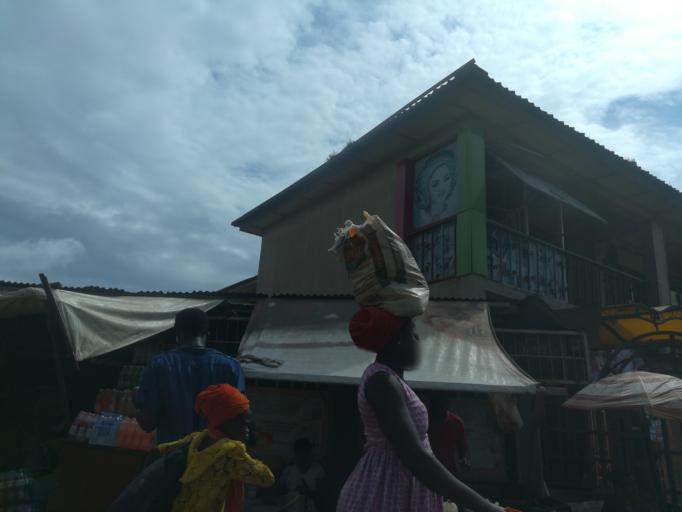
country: NG
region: Lagos
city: Agege
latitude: 6.6262
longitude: 3.3258
